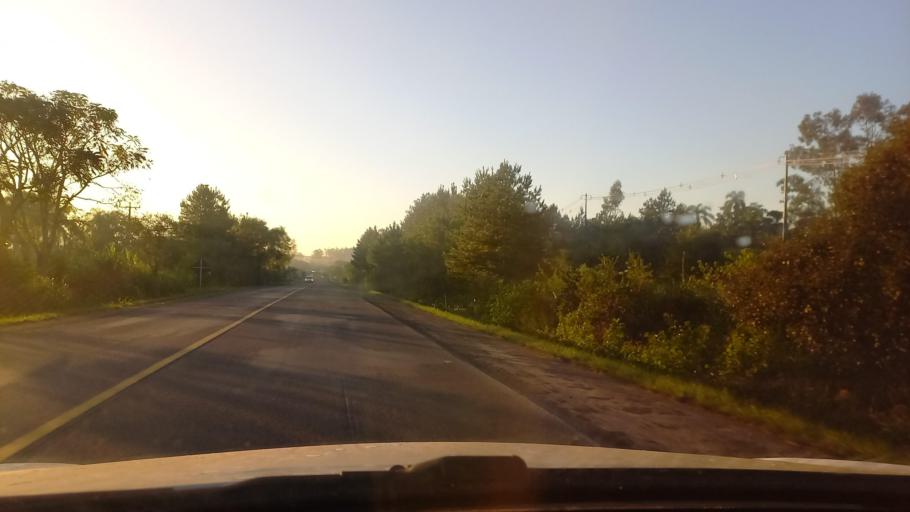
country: BR
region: Rio Grande do Sul
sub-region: Candelaria
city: Candelaria
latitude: -29.6811
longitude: -52.8208
